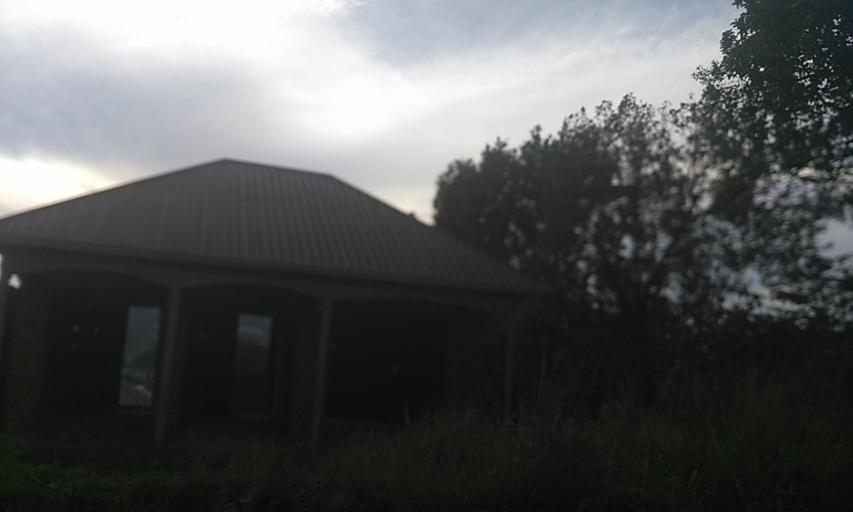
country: UG
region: Central Region
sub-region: Wakiso District
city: Kajansi
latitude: 0.2472
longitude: 32.5014
